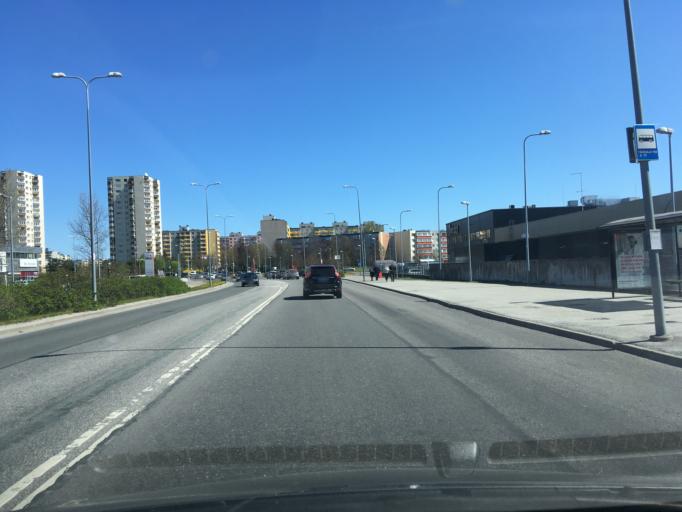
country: EE
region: Harju
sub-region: Tallinna linn
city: Kose
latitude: 59.4438
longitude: 24.8616
